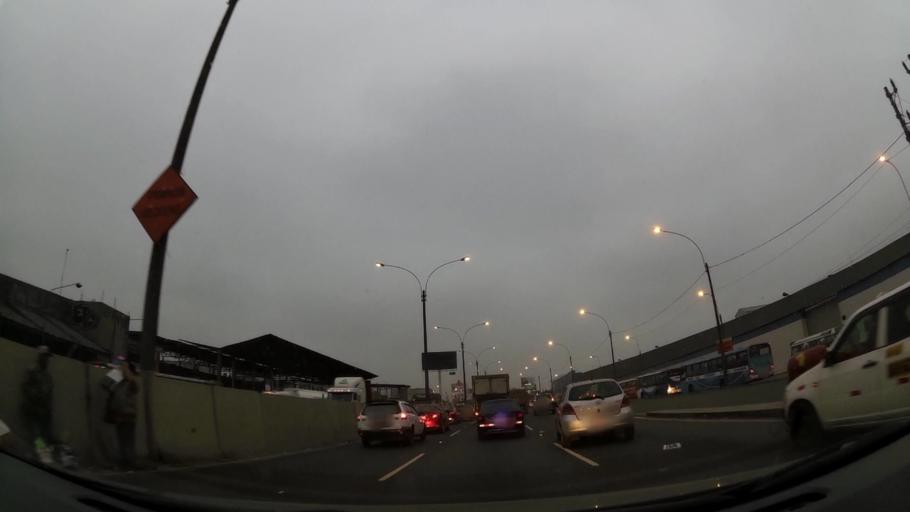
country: PE
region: Lima
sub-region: Lima
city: Independencia
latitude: -12.0113
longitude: -77.0607
